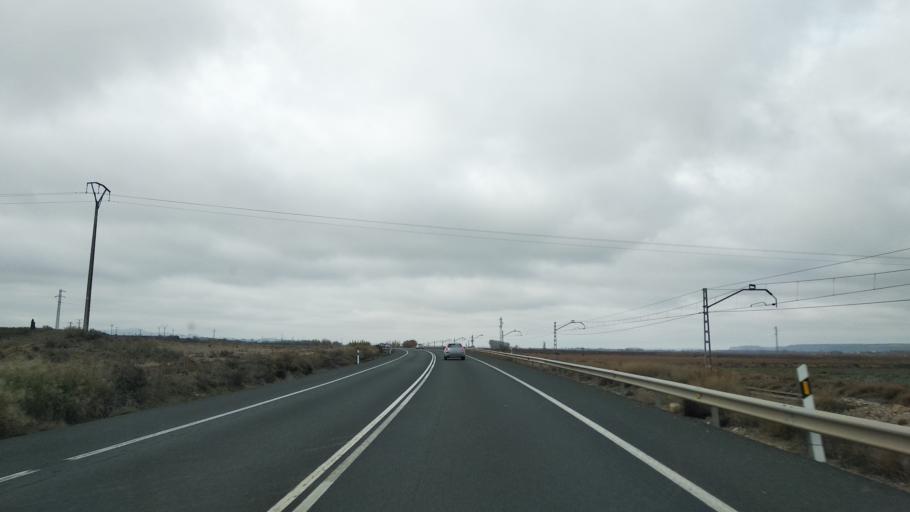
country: ES
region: La Rioja
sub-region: Provincia de La Rioja
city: Rincon de Soto
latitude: 42.2117
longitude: -1.8097
